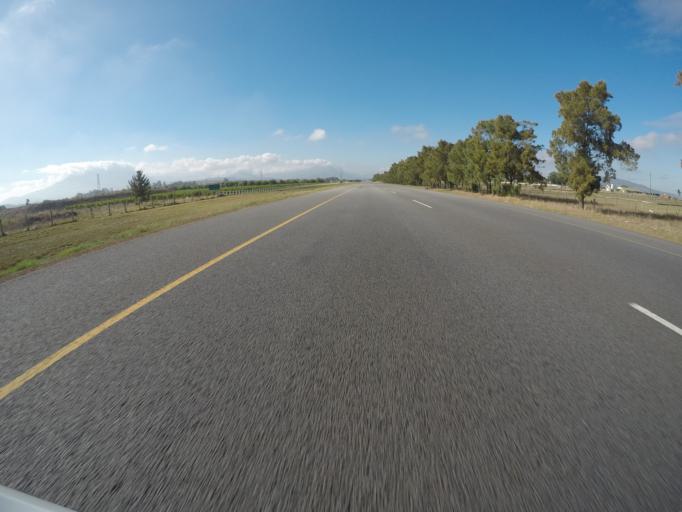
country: ZA
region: Western Cape
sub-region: City of Cape Town
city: Kraaifontein
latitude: -33.8443
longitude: 18.8020
